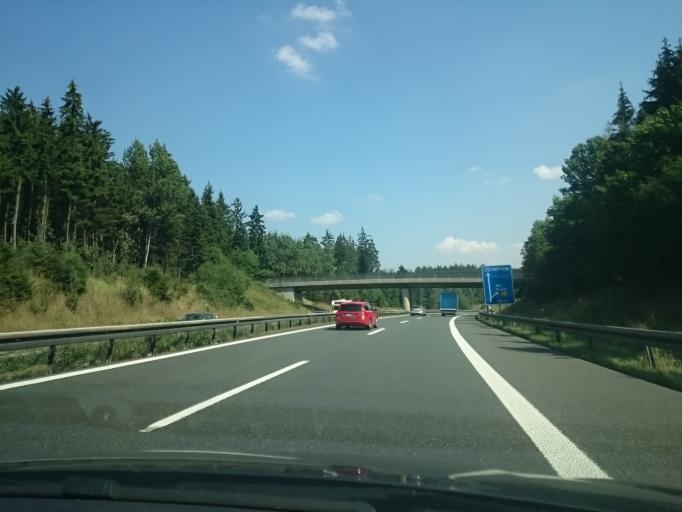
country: DE
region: Bavaria
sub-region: Upper Franconia
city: Koditz
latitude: 50.3390
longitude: 11.8185
